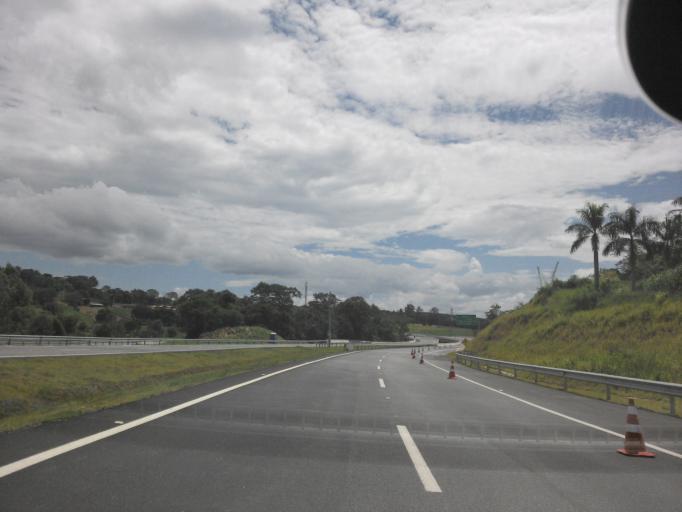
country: BR
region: Sao Paulo
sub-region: Taubate
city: Taubate
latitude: -23.0977
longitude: -45.6074
